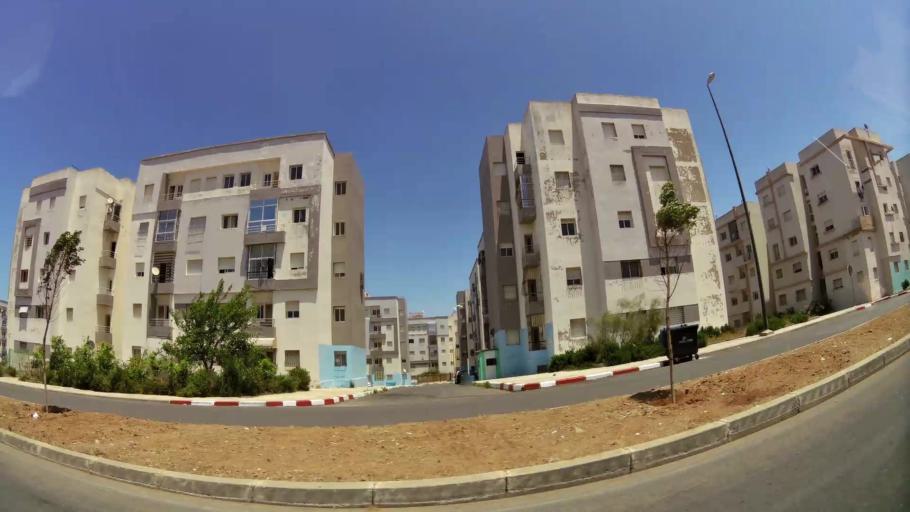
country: MA
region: Gharb-Chrarda-Beni Hssen
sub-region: Kenitra Province
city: Kenitra
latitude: 34.2504
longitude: -6.6430
